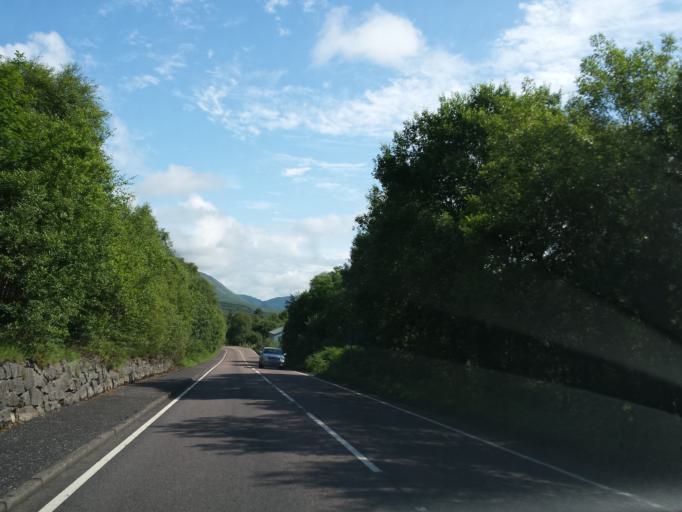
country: GB
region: Scotland
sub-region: Argyll and Bute
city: Garelochhead
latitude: 56.4070
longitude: -5.0333
